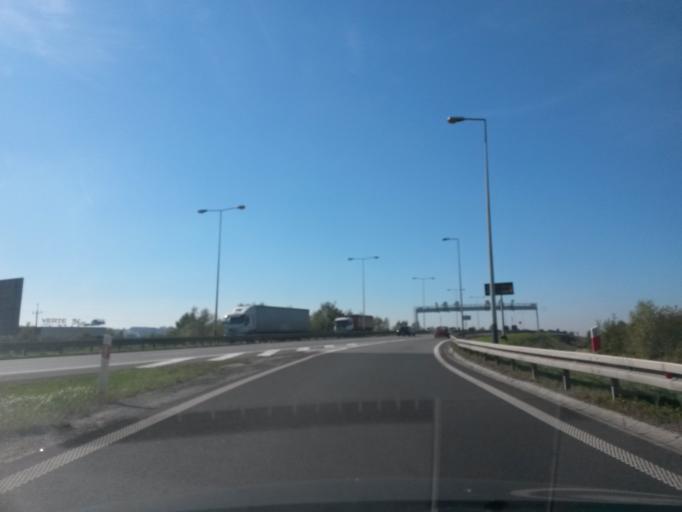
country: PL
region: Lesser Poland Voivodeship
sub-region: Powiat krakowski
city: Libertow
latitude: 49.9917
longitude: 19.9100
